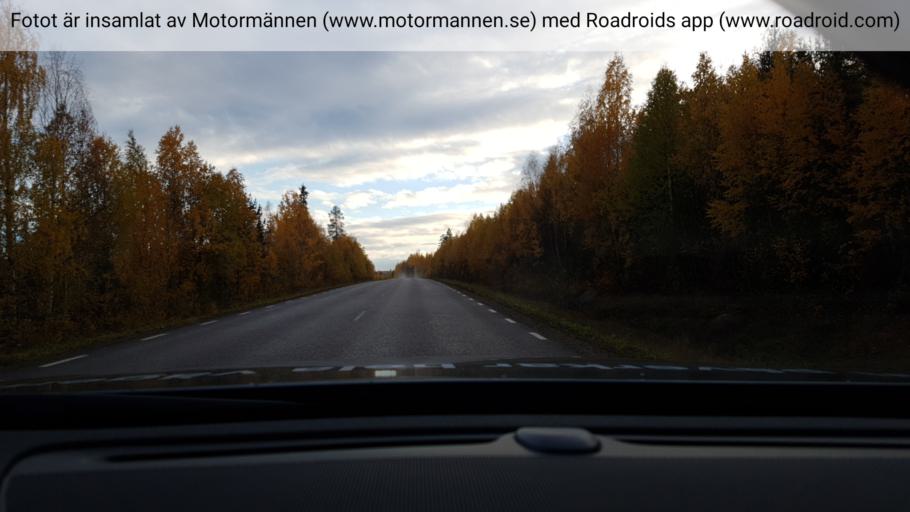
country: SE
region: Norrbotten
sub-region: Overkalix Kommun
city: OEverkalix
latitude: 66.8281
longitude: 22.7523
